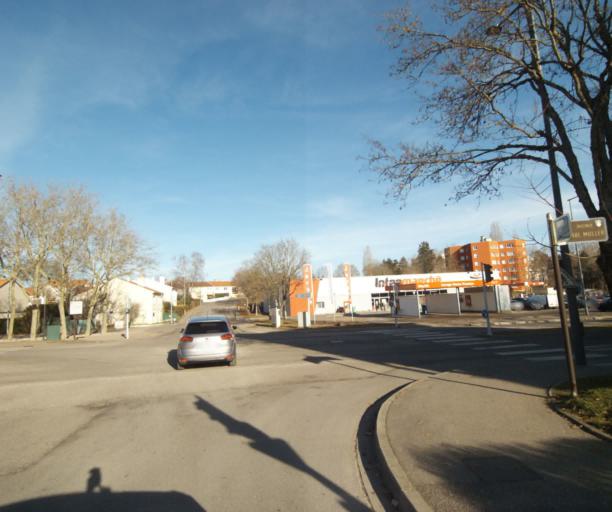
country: FR
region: Lorraine
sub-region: Departement de Meurthe-et-Moselle
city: Chavigny
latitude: 48.6570
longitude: 6.1120
